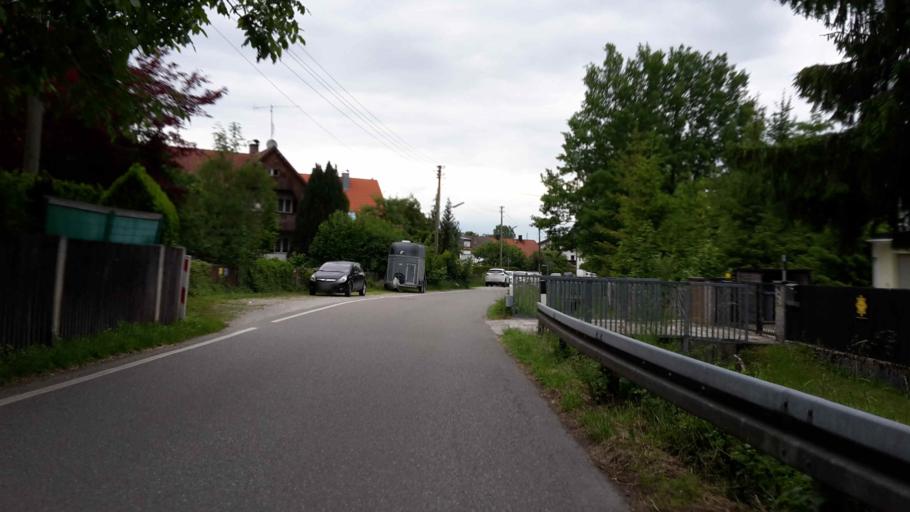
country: DE
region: Bavaria
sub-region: Upper Bavaria
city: Pasing
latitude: 48.1699
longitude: 11.4152
